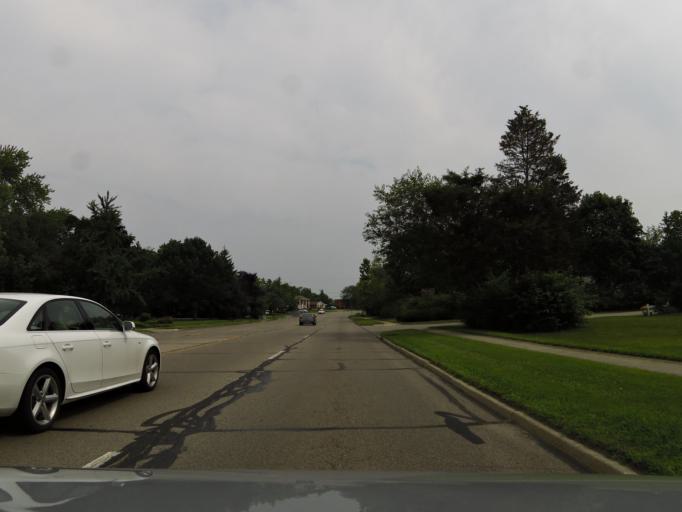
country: US
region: Ohio
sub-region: Montgomery County
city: Kettering
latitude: 39.6932
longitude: -84.1273
